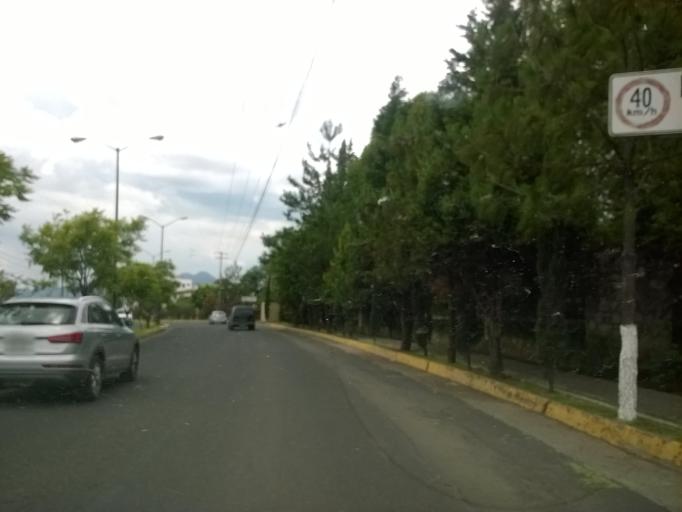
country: MX
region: Michoacan
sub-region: Morelia
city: Montana Monarca (Punta Altozano)
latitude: 19.6741
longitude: -101.1763
